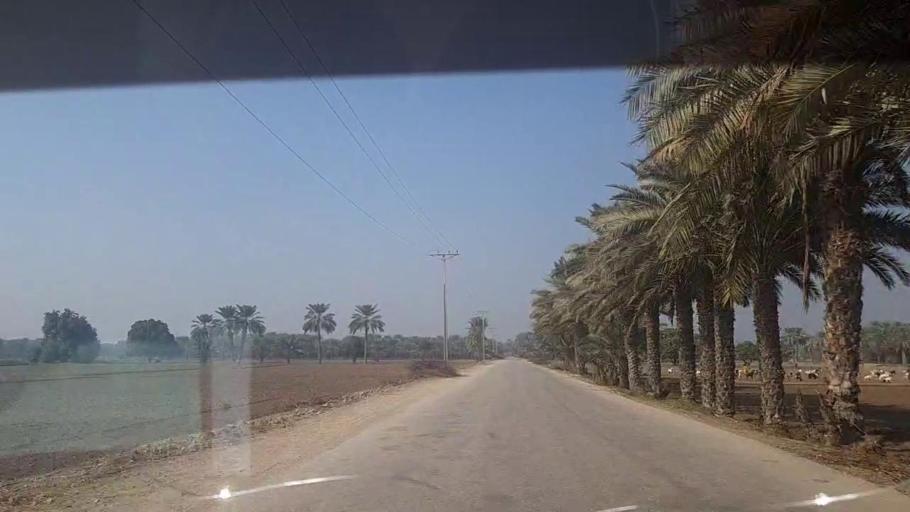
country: PK
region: Sindh
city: Kot Diji
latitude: 27.3748
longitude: 68.6960
